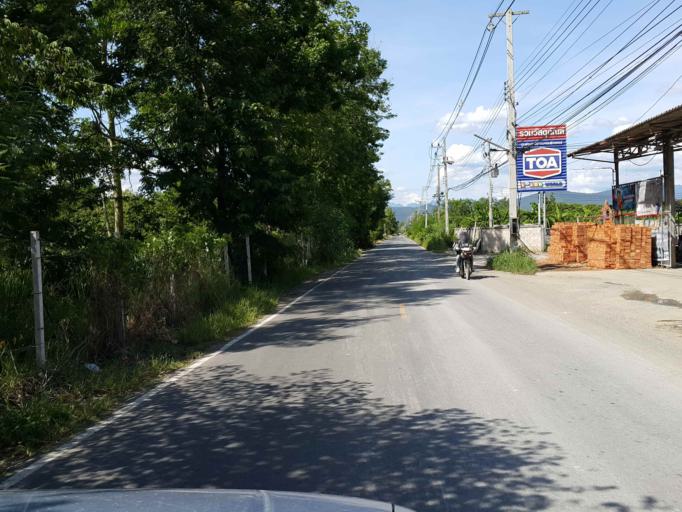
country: TH
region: Chiang Mai
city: San Kamphaeng
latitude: 18.7622
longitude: 99.1424
